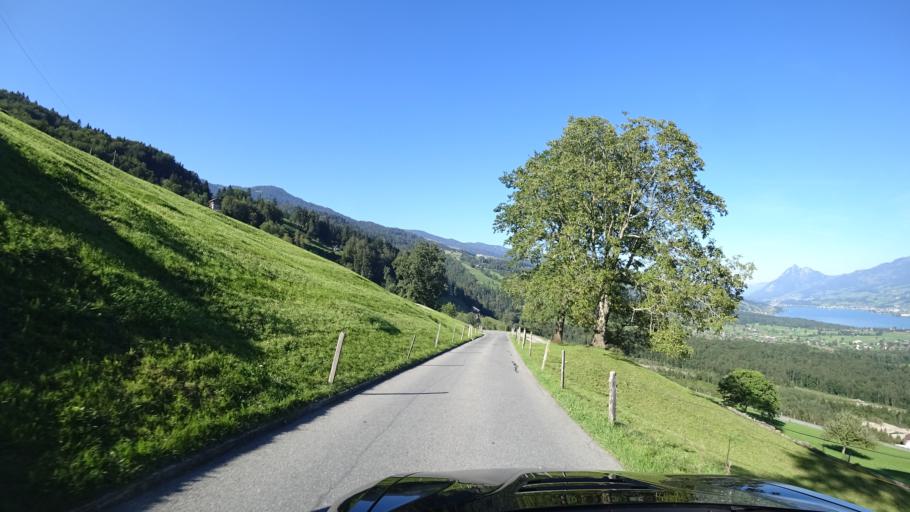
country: CH
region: Obwalden
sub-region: Obwalden
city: Giswil
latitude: 46.8387
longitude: 8.1453
